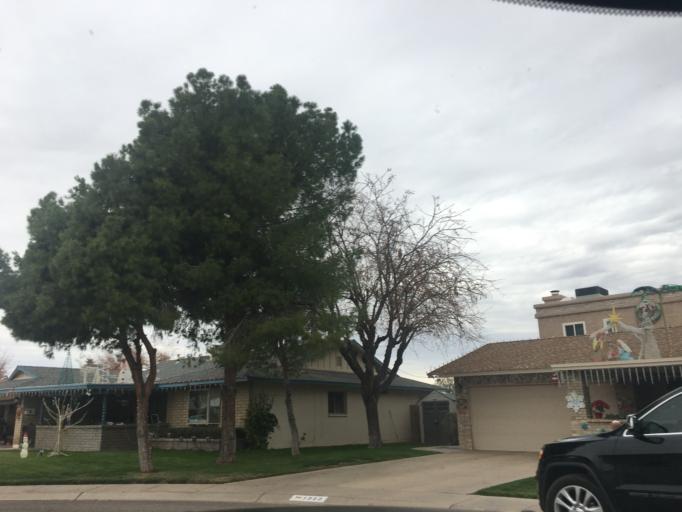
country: US
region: Arizona
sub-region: Maricopa County
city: Tempe
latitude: 33.3797
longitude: -111.9165
